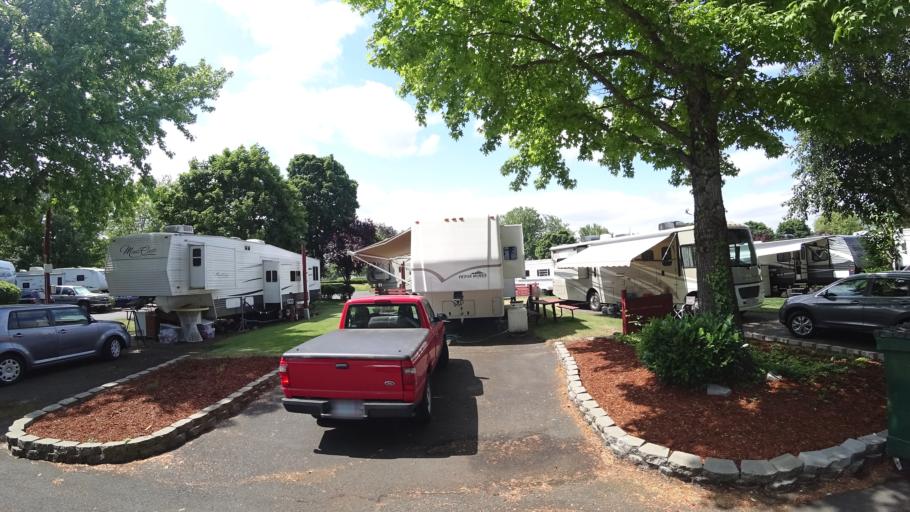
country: US
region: Washington
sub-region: Clark County
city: Vancouver
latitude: 45.6162
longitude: -122.6887
